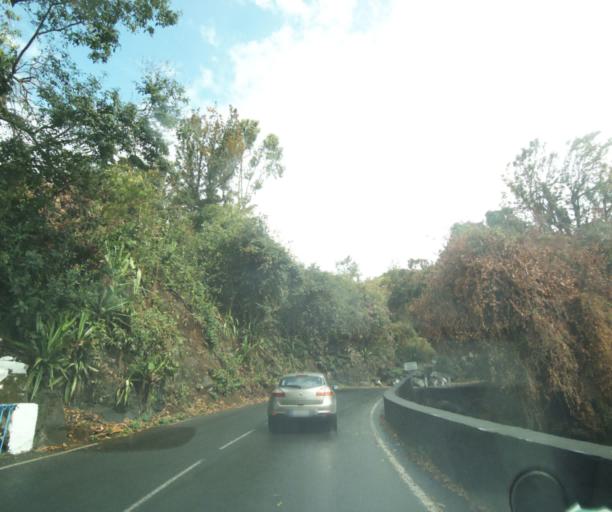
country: RE
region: Reunion
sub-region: Reunion
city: Saint-Paul
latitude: -20.9969
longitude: 55.3286
